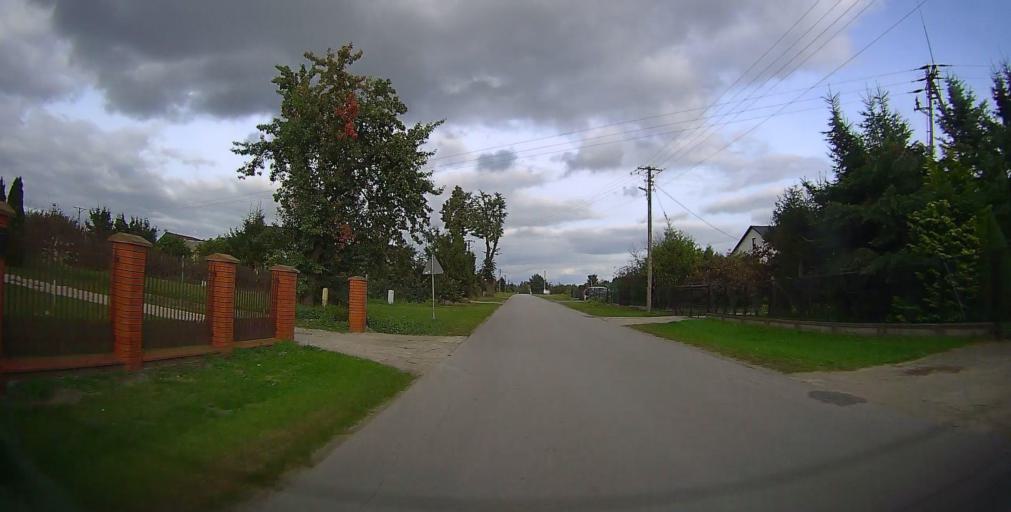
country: PL
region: Masovian Voivodeship
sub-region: Powiat grojecki
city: Jasieniec
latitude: 51.7575
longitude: 20.9244
